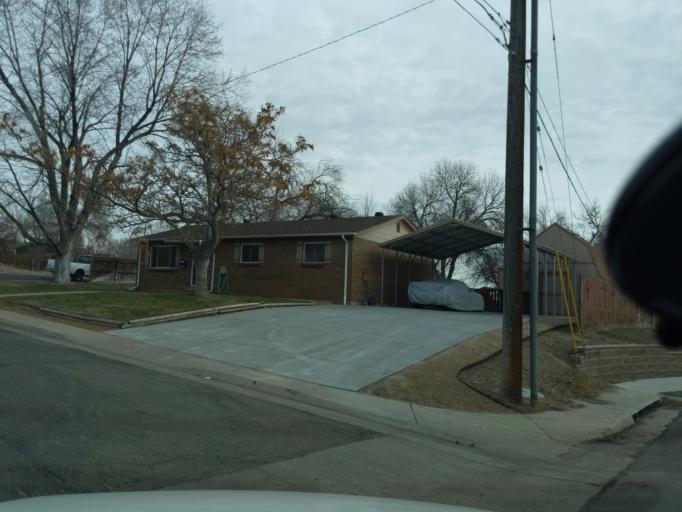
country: US
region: Colorado
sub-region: Adams County
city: Thornton
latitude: 39.8600
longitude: -104.9558
